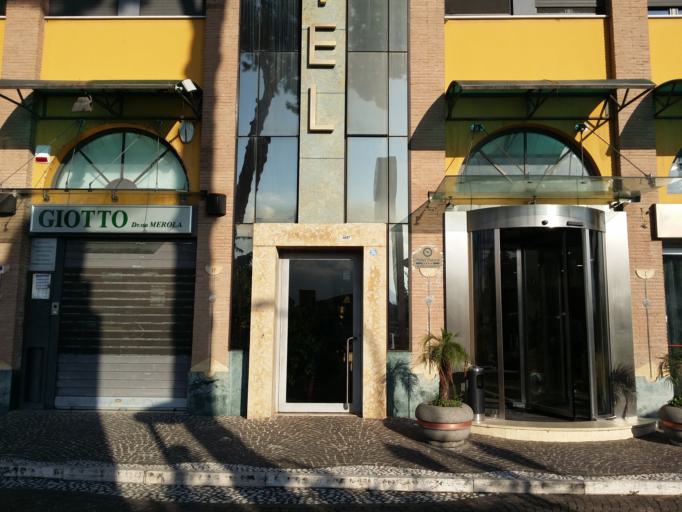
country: IT
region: Campania
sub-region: Provincia di Napoli
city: Arpino
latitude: 40.8906
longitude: 14.3229
